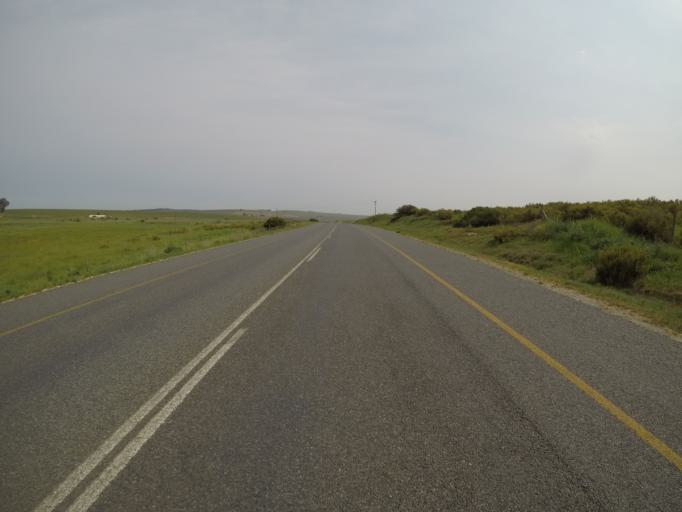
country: ZA
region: Western Cape
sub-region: West Coast District Municipality
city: Malmesbury
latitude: -33.4525
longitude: 18.7782
